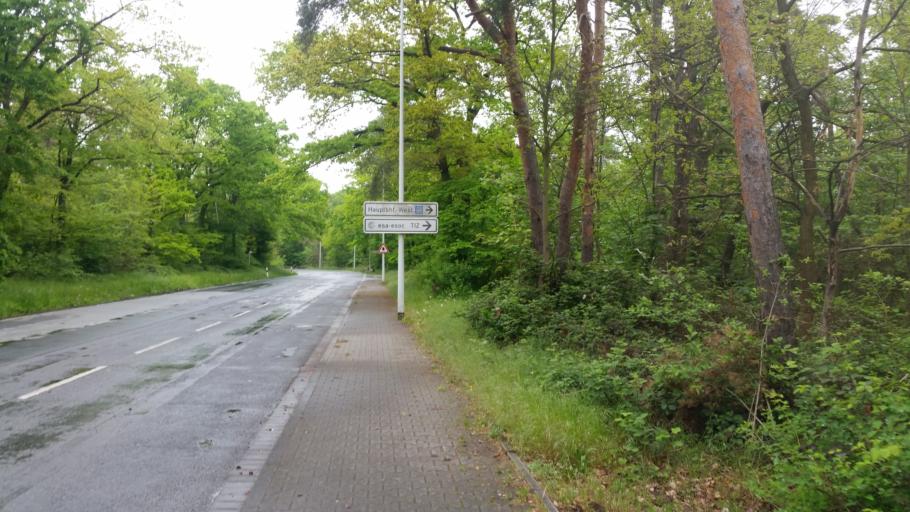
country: DE
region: Hesse
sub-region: Regierungsbezirk Darmstadt
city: Darmstadt
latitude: 49.8695
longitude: 8.6212
